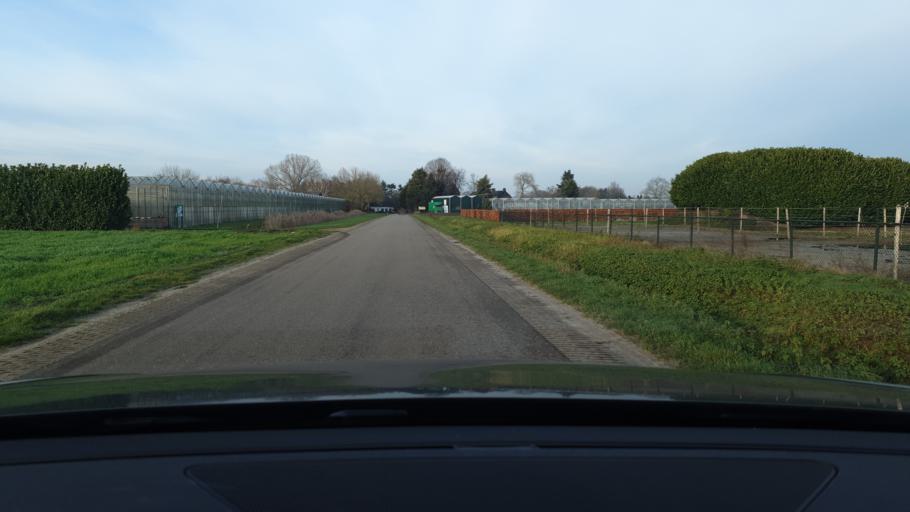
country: NL
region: Limburg
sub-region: Gemeente Venray
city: Venray
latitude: 51.4643
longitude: 6.0375
